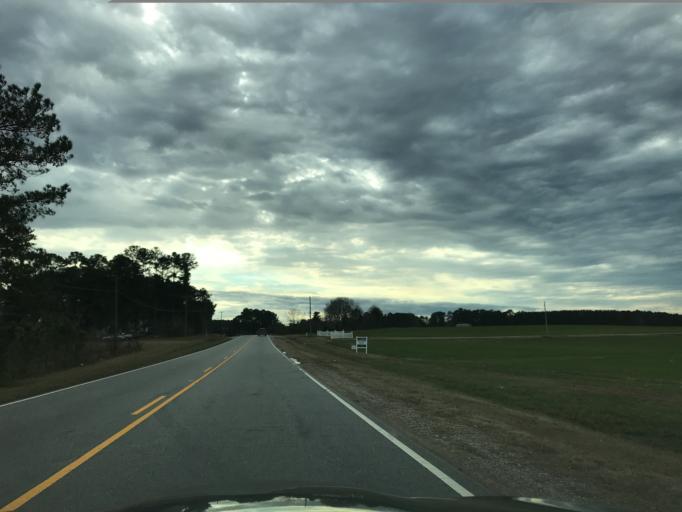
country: US
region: North Carolina
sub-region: Franklin County
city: Louisburg
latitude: 36.1345
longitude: -78.2949
